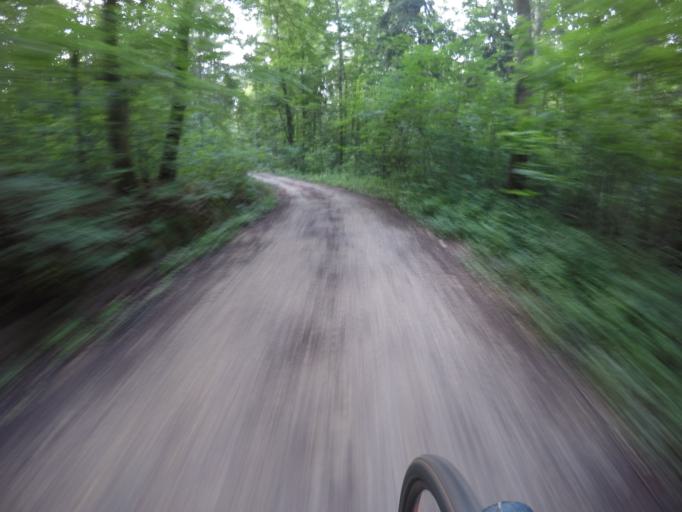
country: DE
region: Baden-Wuerttemberg
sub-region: Regierungsbezirk Stuttgart
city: Schlaitdorf
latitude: 48.6162
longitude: 9.2133
